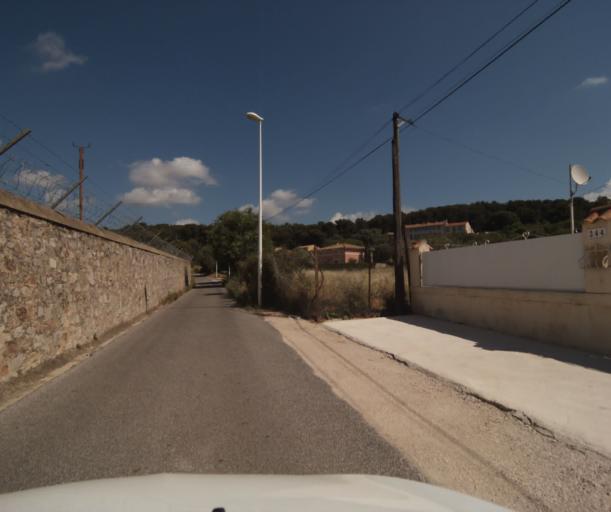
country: FR
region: Provence-Alpes-Cote d'Azur
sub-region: Departement du Var
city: La Seyne-sur-Mer
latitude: 43.1217
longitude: 5.8859
